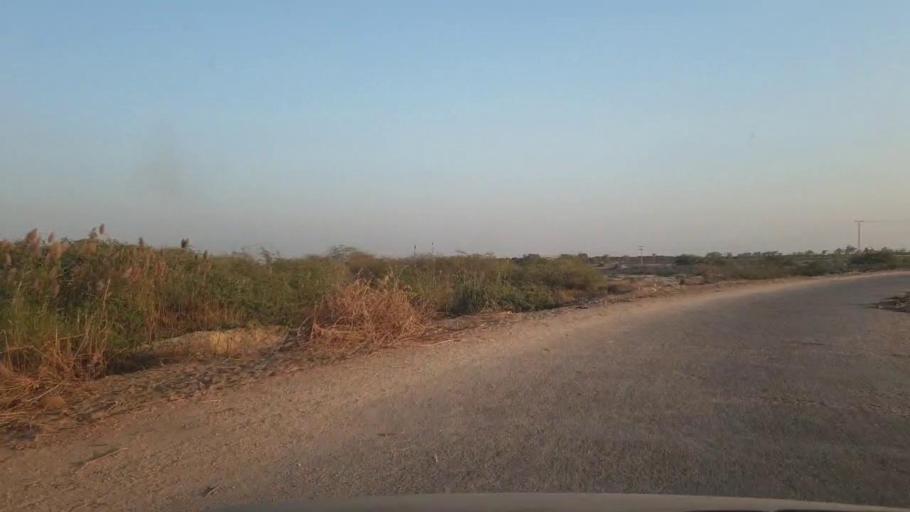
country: PK
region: Sindh
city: Mirwah Gorchani
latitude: 25.2790
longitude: 68.9393
